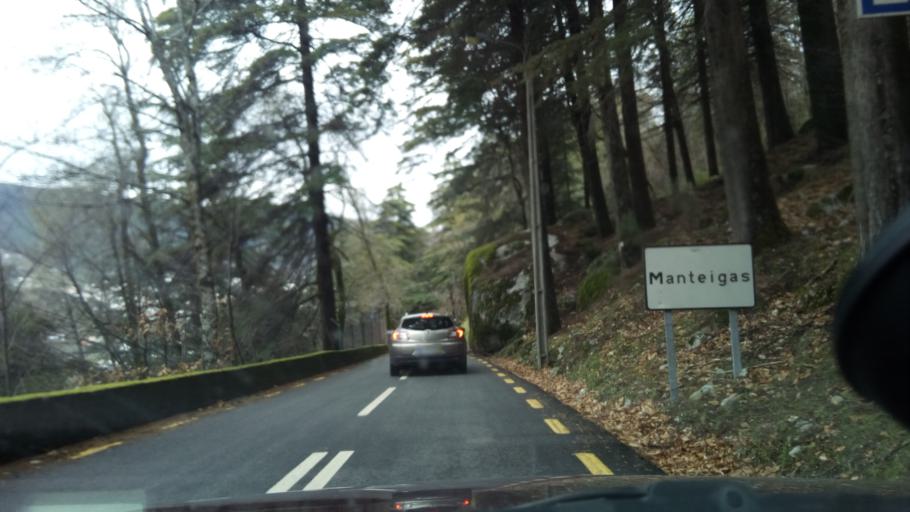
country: PT
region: Guarda
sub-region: Manteigas
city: Manteigas
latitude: 40.3821
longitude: -7.5439
